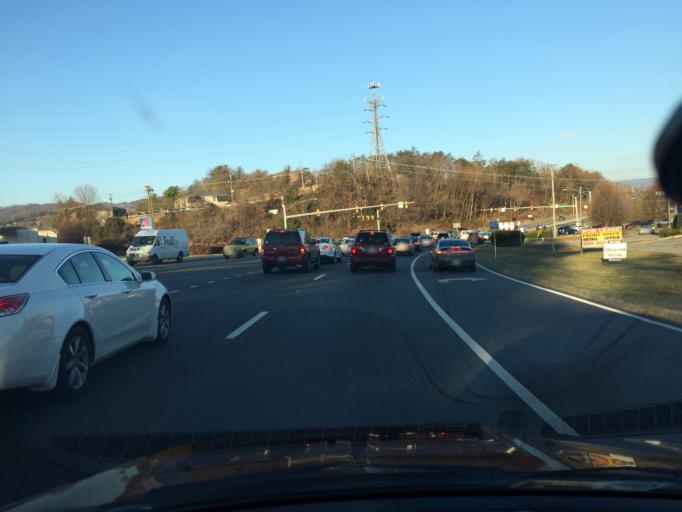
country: US
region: Virginia
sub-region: Roanoke County
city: Cave Spring
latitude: 37.2294
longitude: -80.0072
